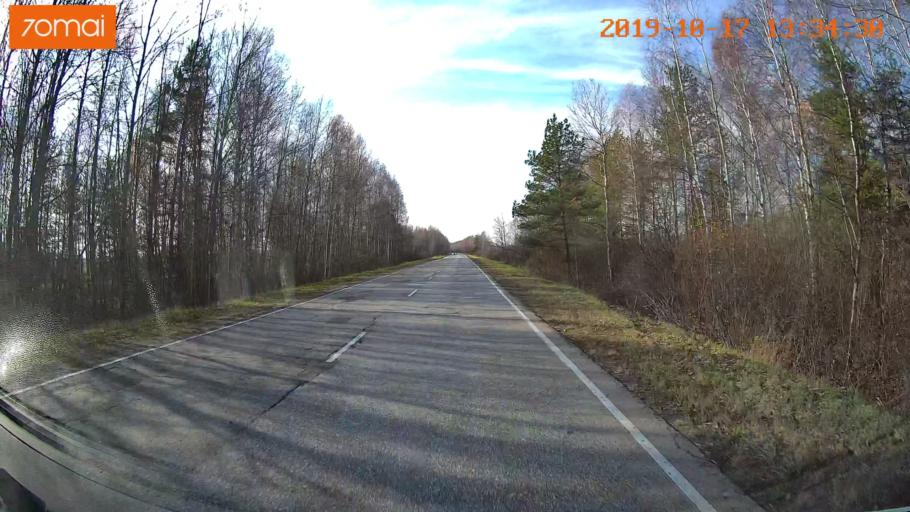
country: RU
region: Vladimir
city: Velikodvorskiy
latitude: 55.1442
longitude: 40.7139
